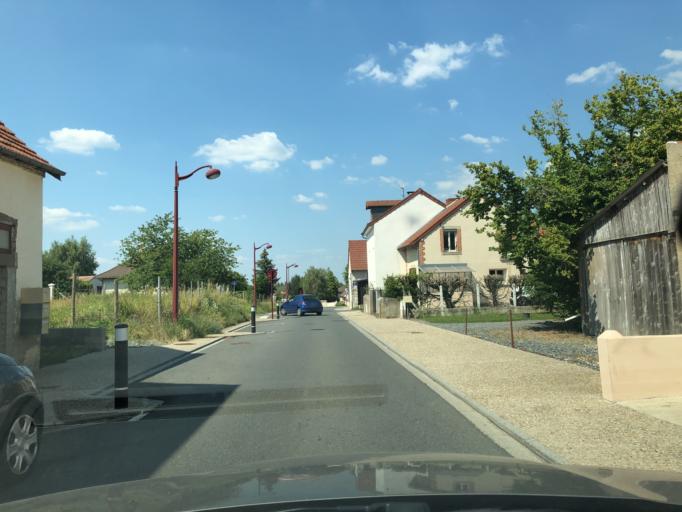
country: FR
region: Auvergne
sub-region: Departement de l'Allier
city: Abrest
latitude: 46.1106
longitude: 3.4628
